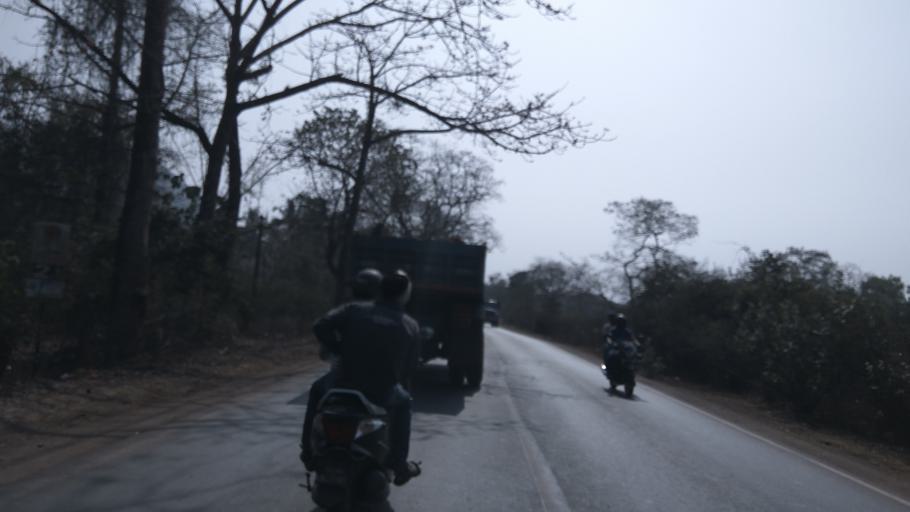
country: IN
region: Goa
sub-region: North Goa
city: Palle
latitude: 15.4058
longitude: 74.0922
